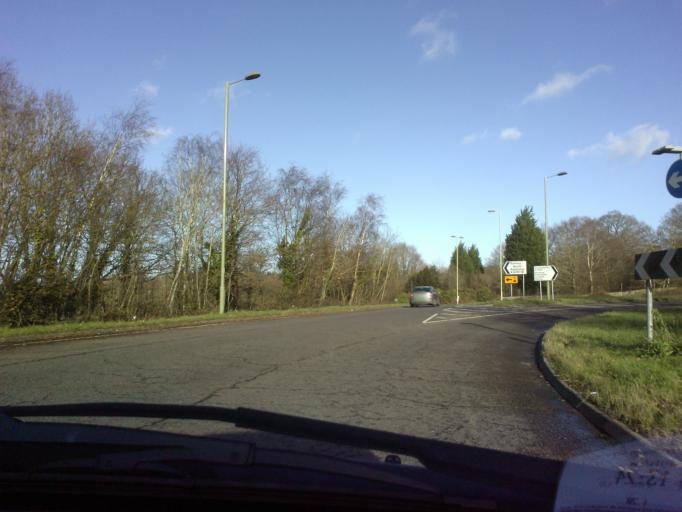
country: GB
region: England
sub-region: Hampshire
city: Totton
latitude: 50.9554
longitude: -1.4734
